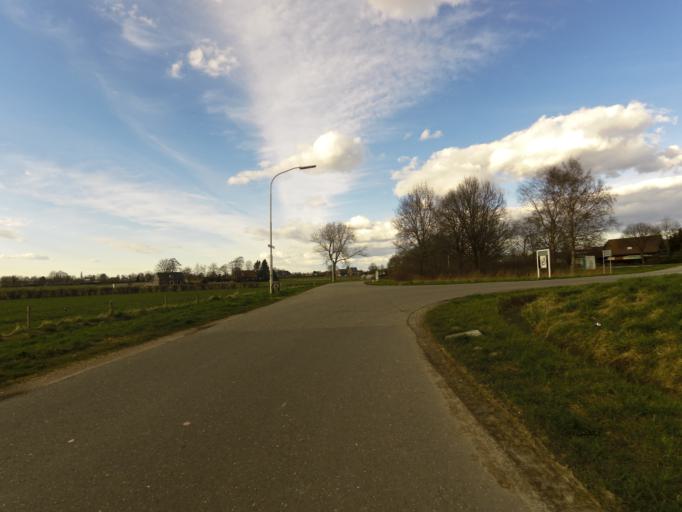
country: NL
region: Gelderland
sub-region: Gemeente Zevenaar
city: Zevenaar
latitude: 51.9450
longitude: 6.1212
